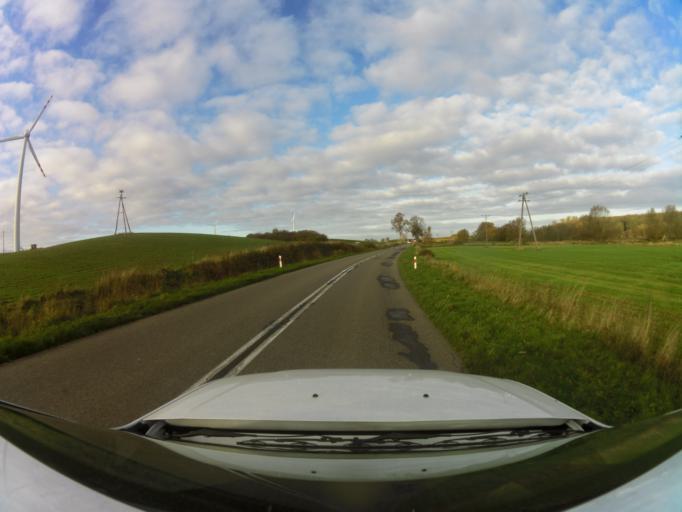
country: PL
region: West Pomeranian Voivodeship
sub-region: Powiat gryficki
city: Cerkwica
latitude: 54.0693
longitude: 15.1110
